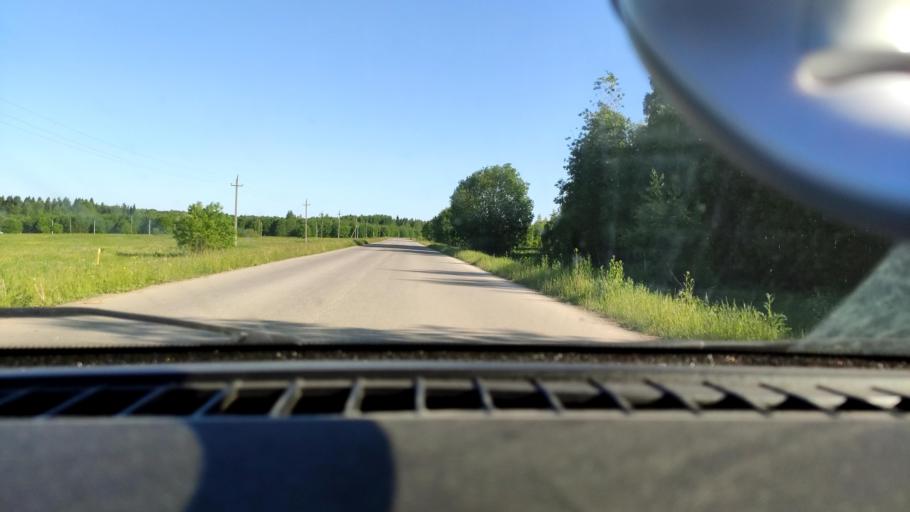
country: RU
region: Perm
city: Polazna
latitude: 58.1963
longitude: 56.5352
